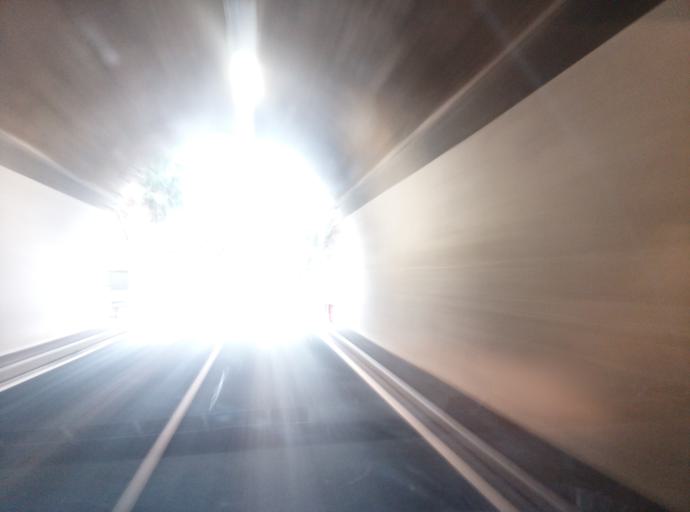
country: SI
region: Idrija
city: Idrija
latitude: 45.9561
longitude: 14.0817
